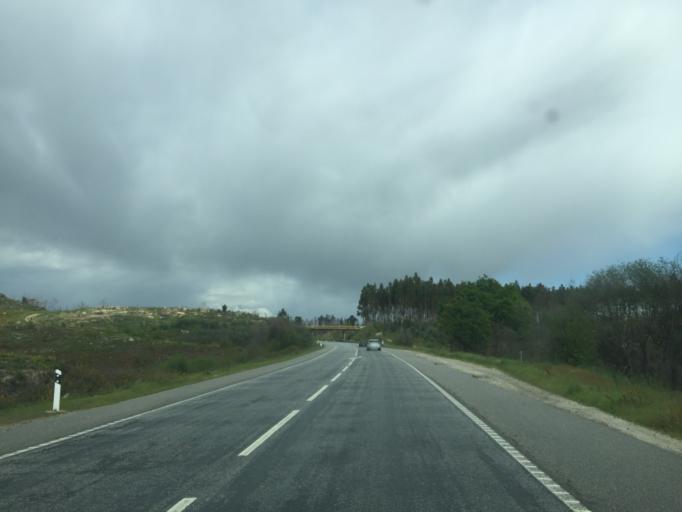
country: PT
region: Viseu
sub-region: Vouzela
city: Vouzela
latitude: 40.6532
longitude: -8.0339
